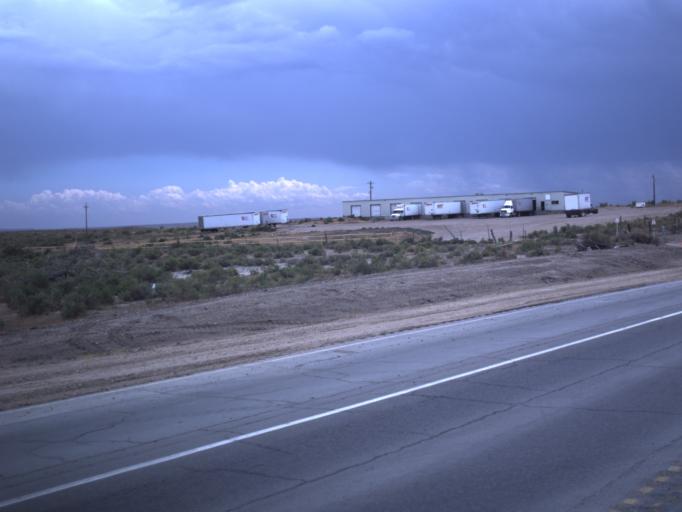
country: US
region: Utah
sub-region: Duchesne County
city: Roosevelt
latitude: 40.2192
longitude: -110.0674
